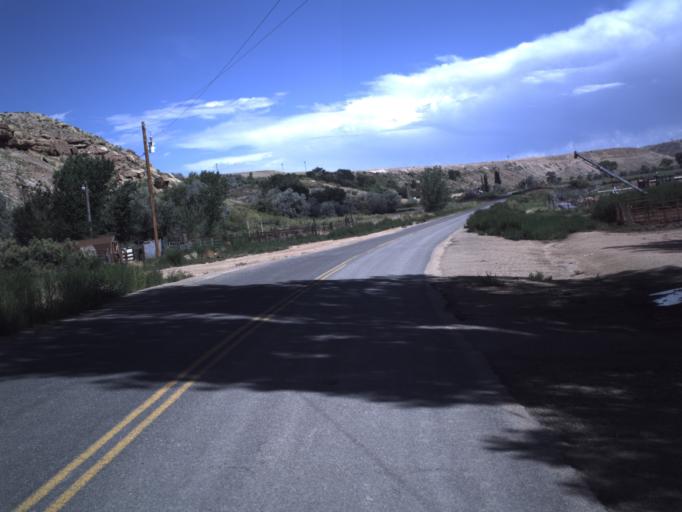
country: US
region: Utah
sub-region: Duchesne County
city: Duchesne
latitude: 40.1737
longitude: -110.4280
